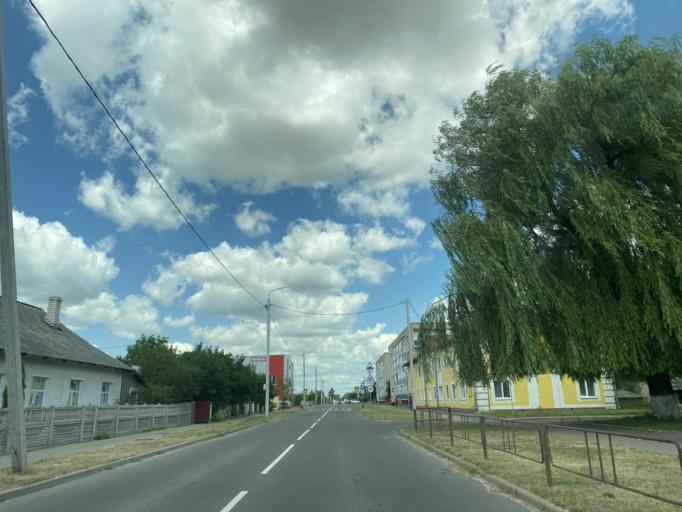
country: BY
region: Brest
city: Ivanava
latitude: 52.1500
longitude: 25.5423
